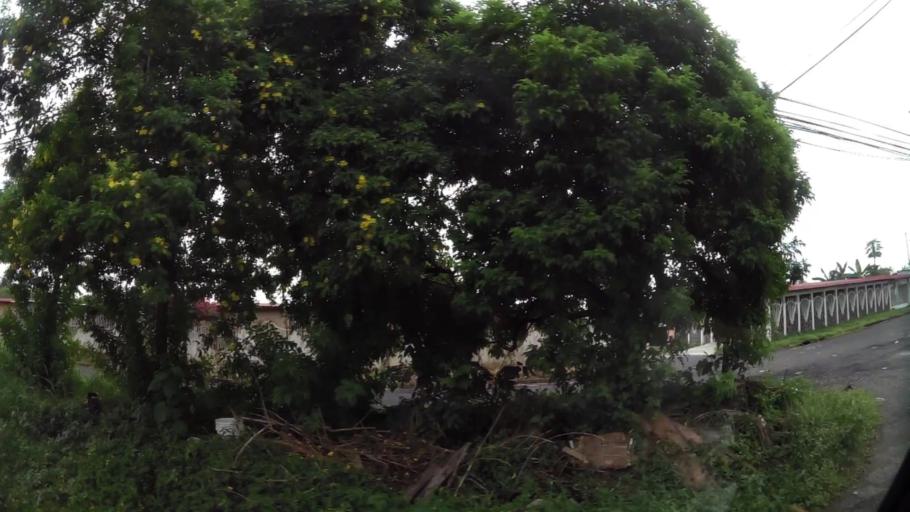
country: PA
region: Panama
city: Cabra Numero Uno
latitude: 9.0959
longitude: -79.3442
